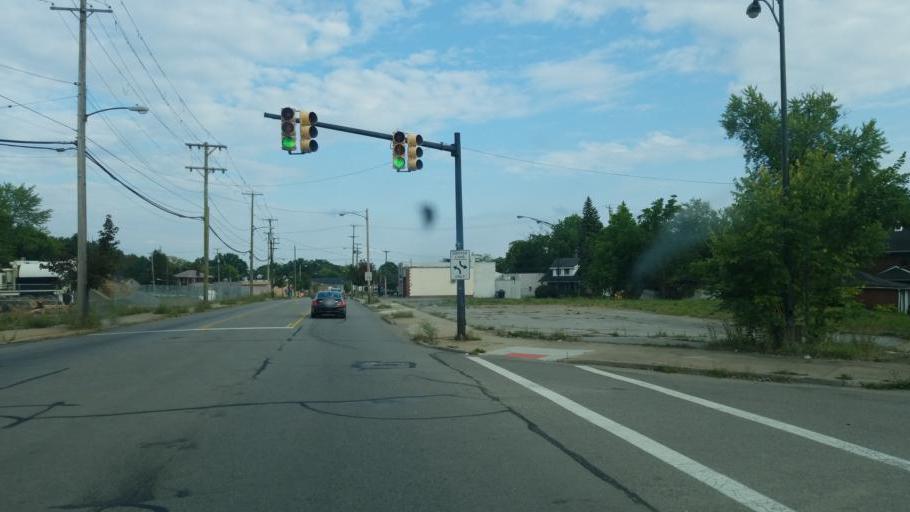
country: US
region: Ohio
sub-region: Mahoning County
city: Youngstown
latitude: 41.1227
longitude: -80.6621
